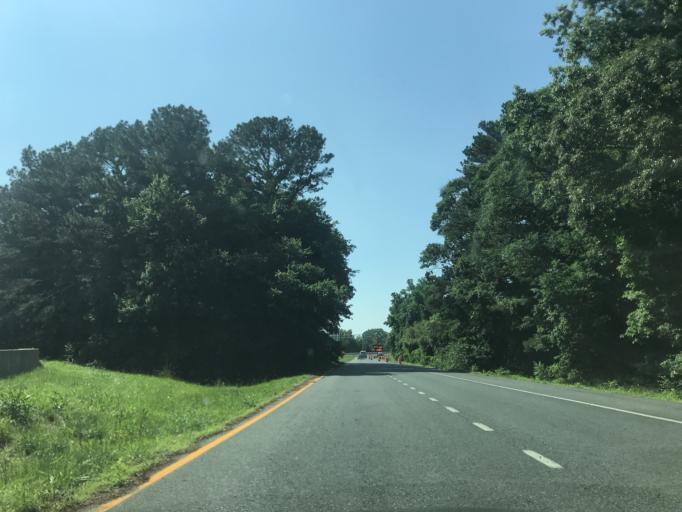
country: US
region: Maryland
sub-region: Wicomico County
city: Salisbury
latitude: 38.3714
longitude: -75.5359
